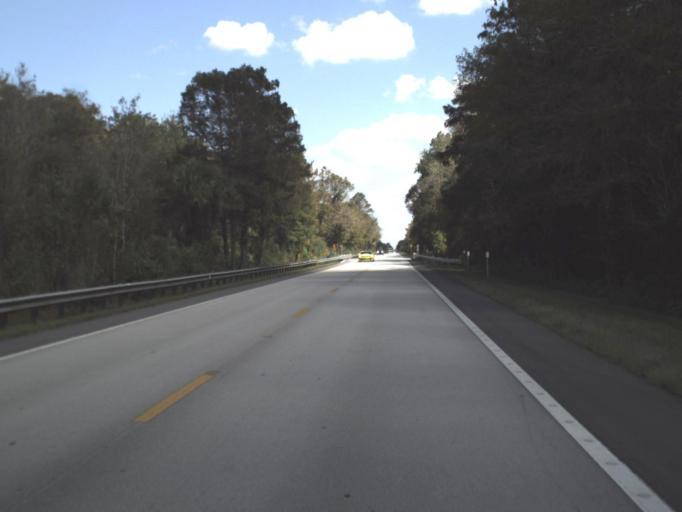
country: US
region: Florida
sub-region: Miami-Dade County
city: Kendall West
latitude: 25.8597
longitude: -81.0614
